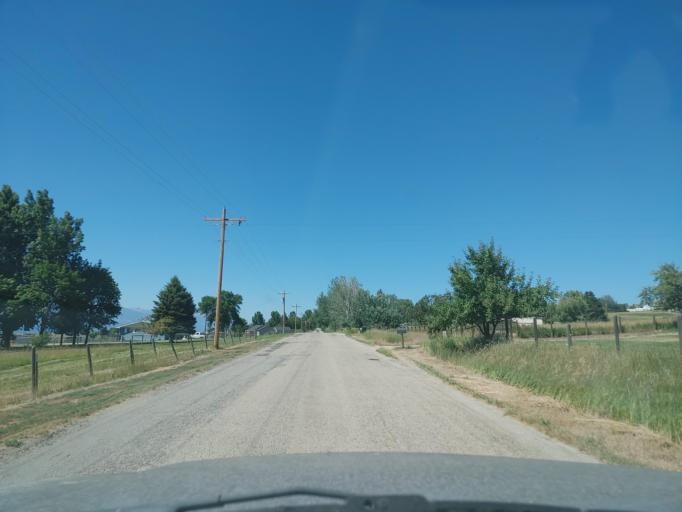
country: US
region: Montana
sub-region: Ravalli County
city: Hamilton
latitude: 46.3367
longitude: -114.0614
